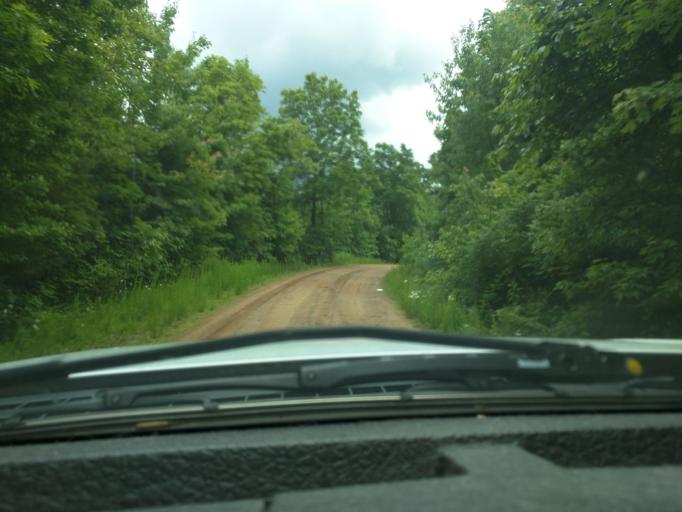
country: US
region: Arkansas
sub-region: Madison County
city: Huntsville
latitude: 35.8835
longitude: -93.5399
